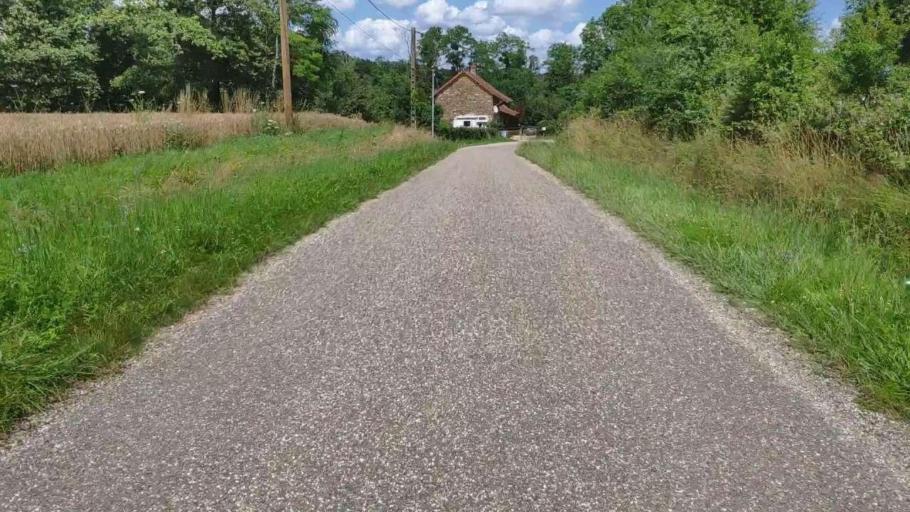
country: FR
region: Franche-Comte
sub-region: Departement du Jura
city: Chaussin
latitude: 46.8879
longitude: 5.4918
